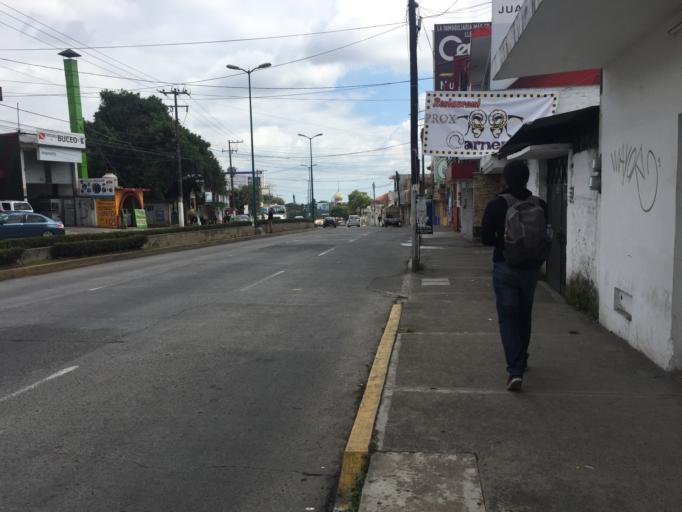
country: MX
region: Veracruz
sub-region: Xalapa
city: Xalapa de Enriquez
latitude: 19.5251
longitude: -96.9025
